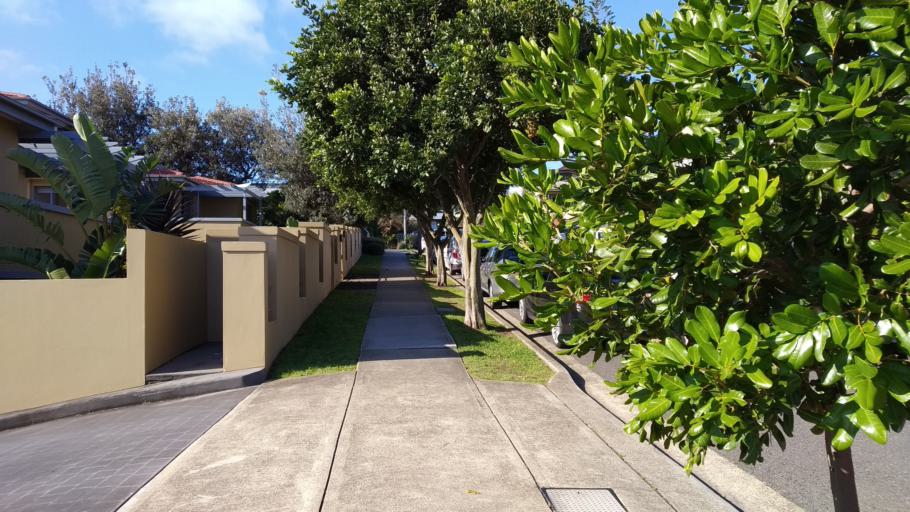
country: AU
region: New South Wales
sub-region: Waverley
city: North Bondi
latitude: -33.8838
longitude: 151.2810
